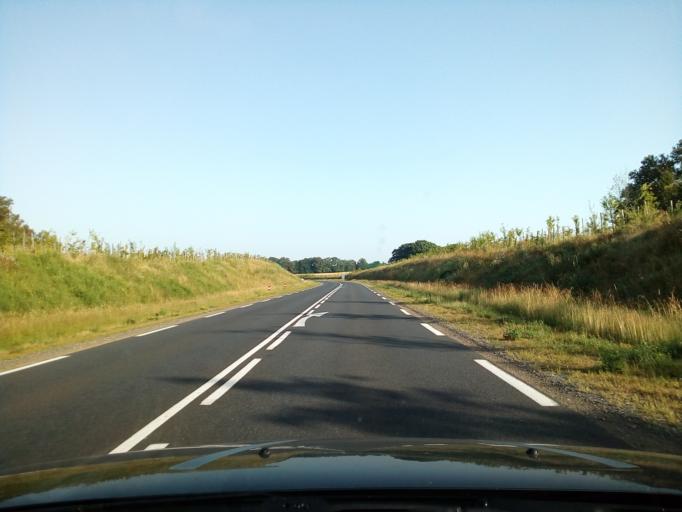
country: FR
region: Limousin
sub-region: Departement de la Haute-Vienne
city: Peyrat-de-Bellac
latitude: 46.1143
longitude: 0.9209
